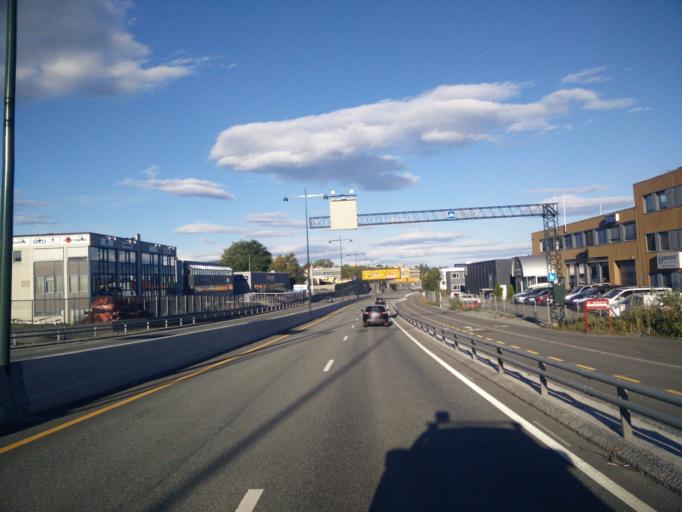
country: NO
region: Sor-Trondelag
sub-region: Trondheim
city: Trondheim
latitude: 63.4322
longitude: 10.4713
